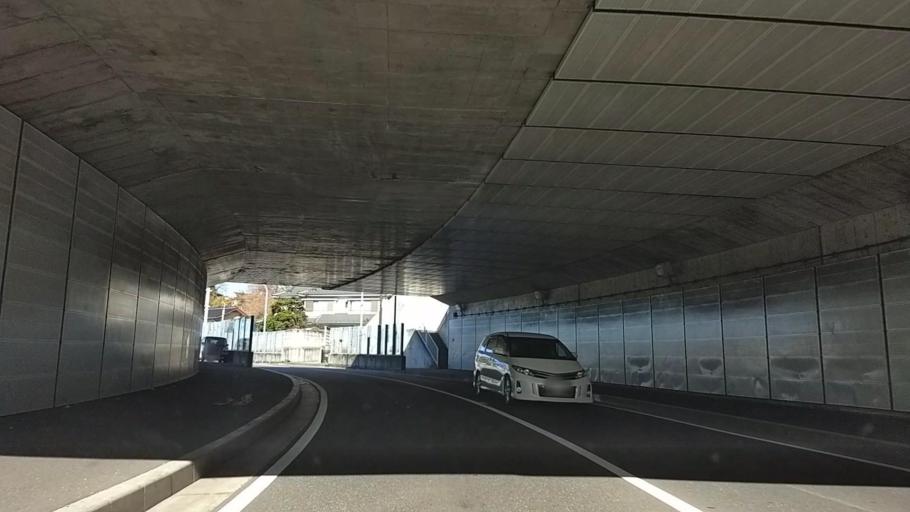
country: JP
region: Kanagawa
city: Yokohama
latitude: 35.4729
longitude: 139.5763
